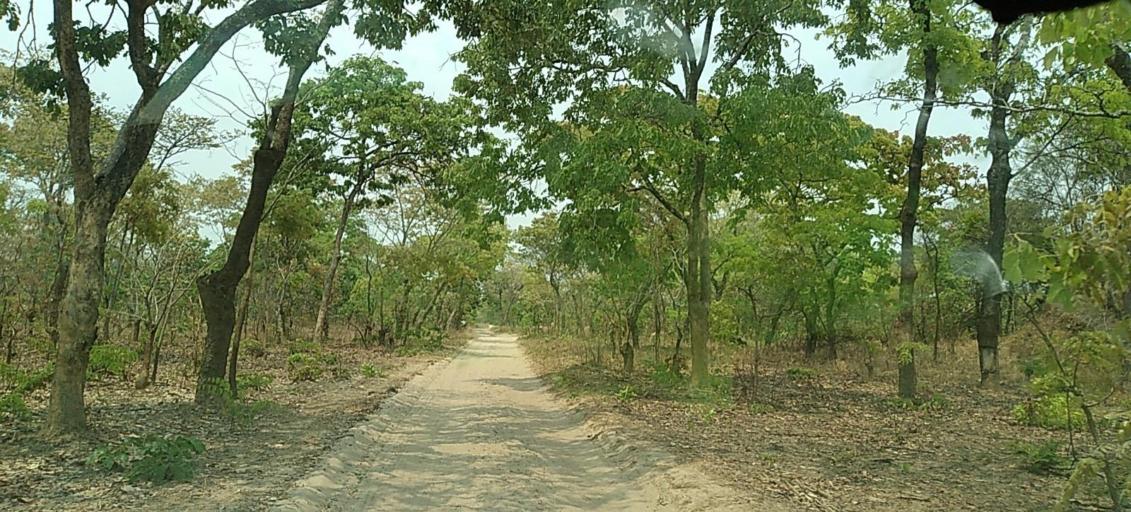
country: ZM
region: North-Western
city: Kabompo
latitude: -13.5539
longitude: 24.4482
